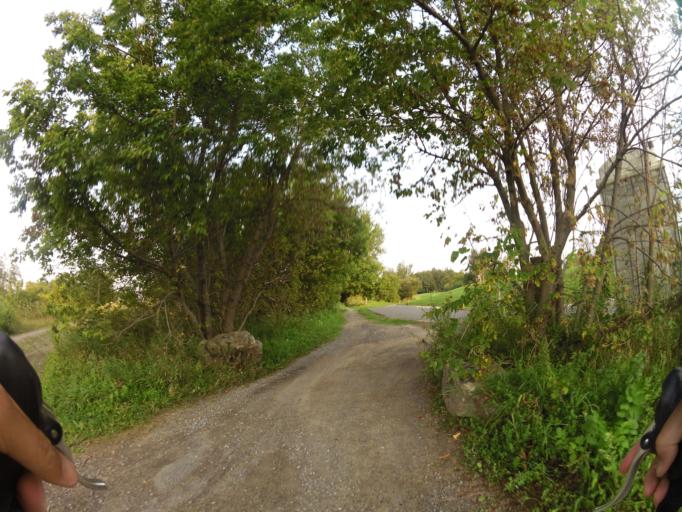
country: CA
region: Ontario
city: Bells Corners
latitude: 45.3493
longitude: -75.8998
